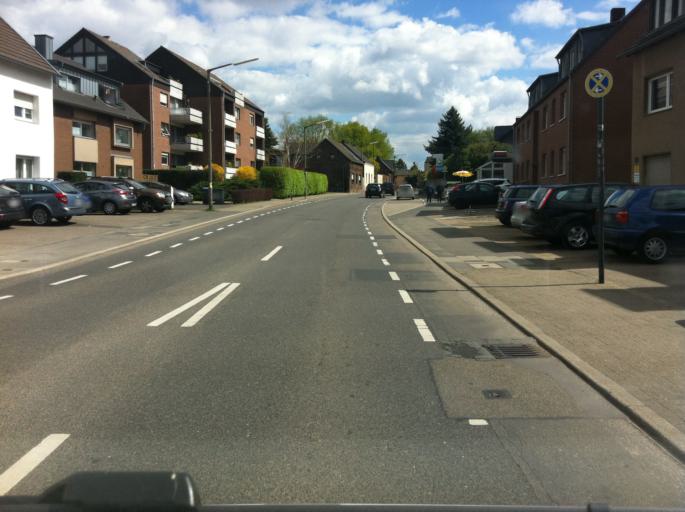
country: DE
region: North Rhine-Westphalia
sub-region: Regierungsbezirk Koln
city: Mengenich
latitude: 51.0139
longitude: 6.8545
